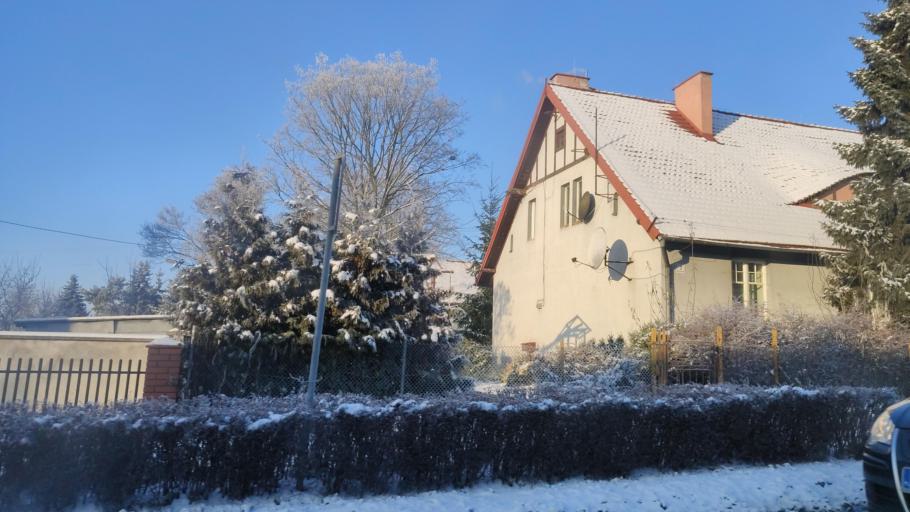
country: PL
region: Kujawsko-Pomorskie
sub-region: Powiat zninski
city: Barcin
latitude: 52.8658
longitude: 17.9459
